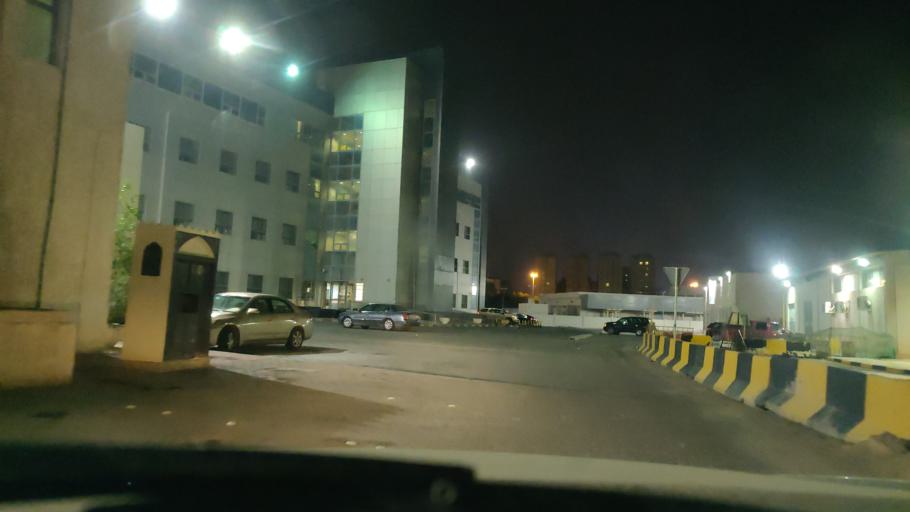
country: KW
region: Muhafazat al Jahra'
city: Al Jahra'
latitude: 29.3385
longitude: 47.6799
